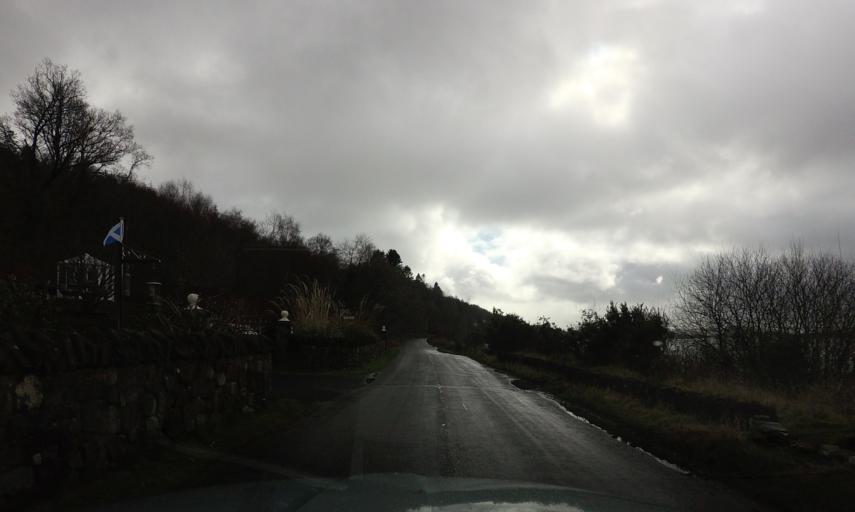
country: GB
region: Scotland
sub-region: West Dunbartonshire
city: Balloch
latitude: 56.1185
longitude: -4.5891
